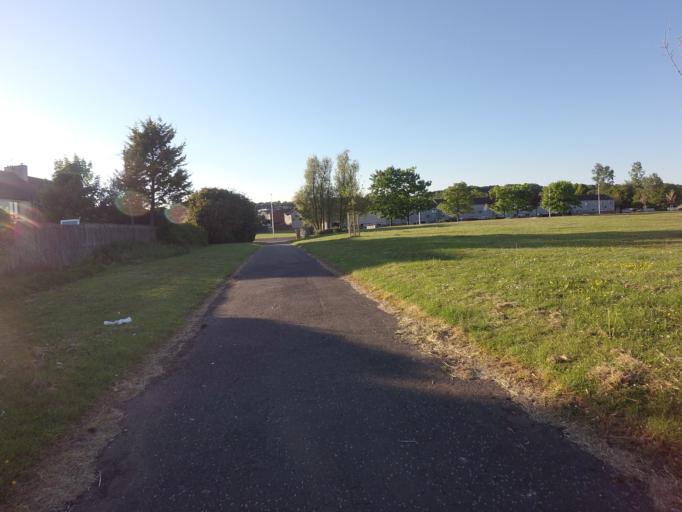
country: GB
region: Scotland
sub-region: West Lothian
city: Livingston
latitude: 55.9015
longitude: -3.5600
